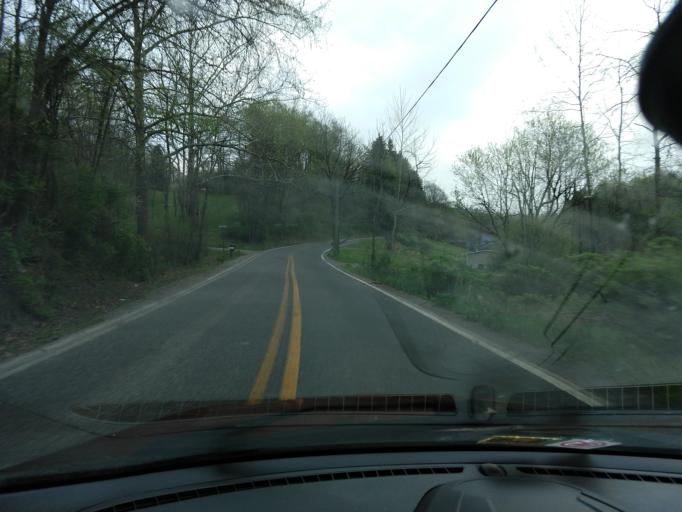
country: US
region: West Virginia
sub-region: Harrison County
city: Bridgeport
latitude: 39.3360
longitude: -80.2769
